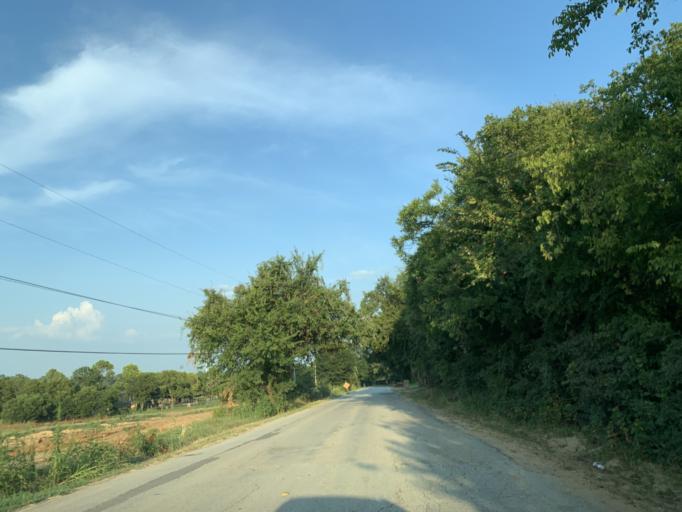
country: US
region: Texas
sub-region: Tarrant County
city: Hurst
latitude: 32.7810
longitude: -97.1907
